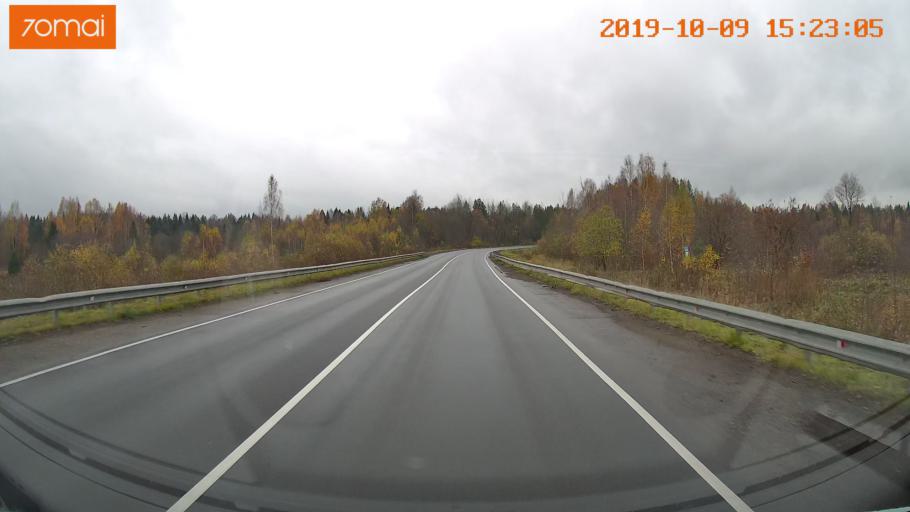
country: RU
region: Kostroma
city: Susanino
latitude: 58.0383
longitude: 41.4870
